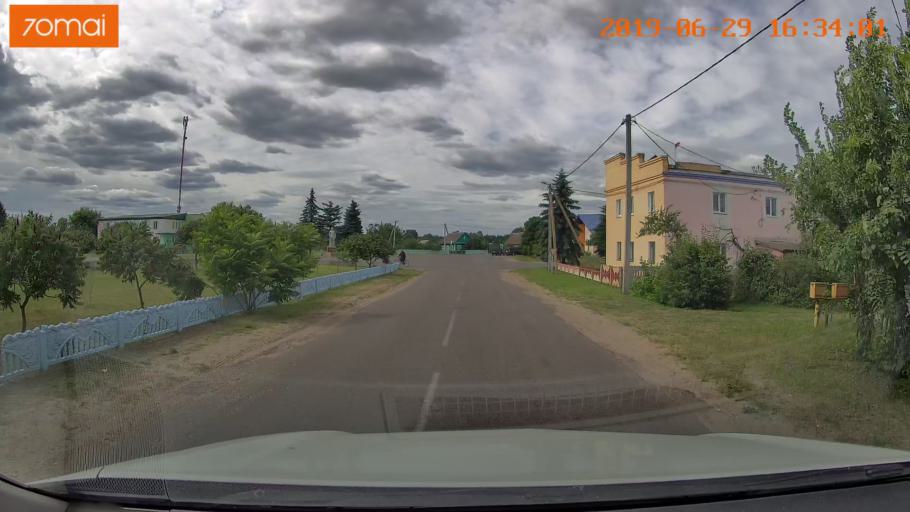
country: BY
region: Brest
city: Luninyets
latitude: 52.2056
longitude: 27.0107
